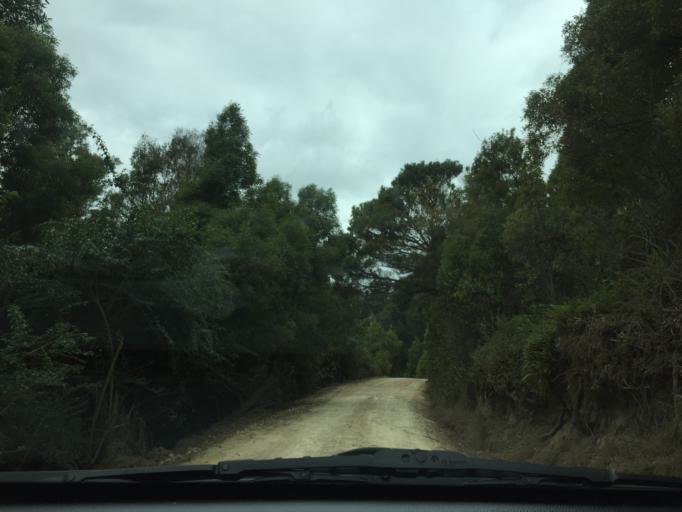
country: CO
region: Cundinamarca
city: Tabio
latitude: 4.9210
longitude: -74.1062
